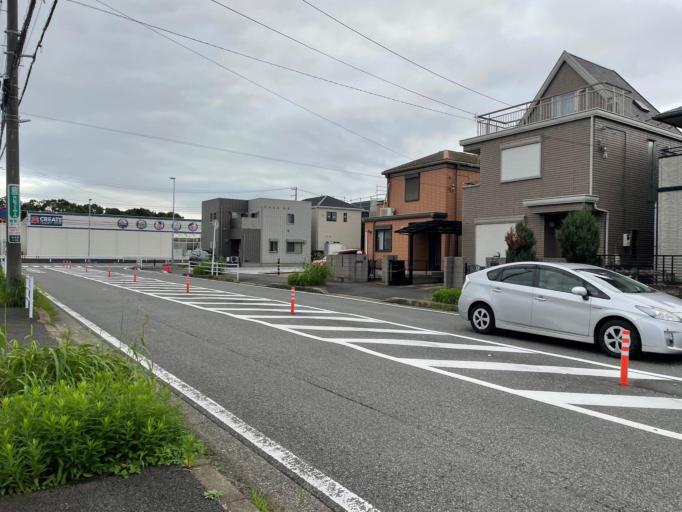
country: JP
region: Chiba
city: Chiba
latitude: 35.6430
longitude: 140.0758
